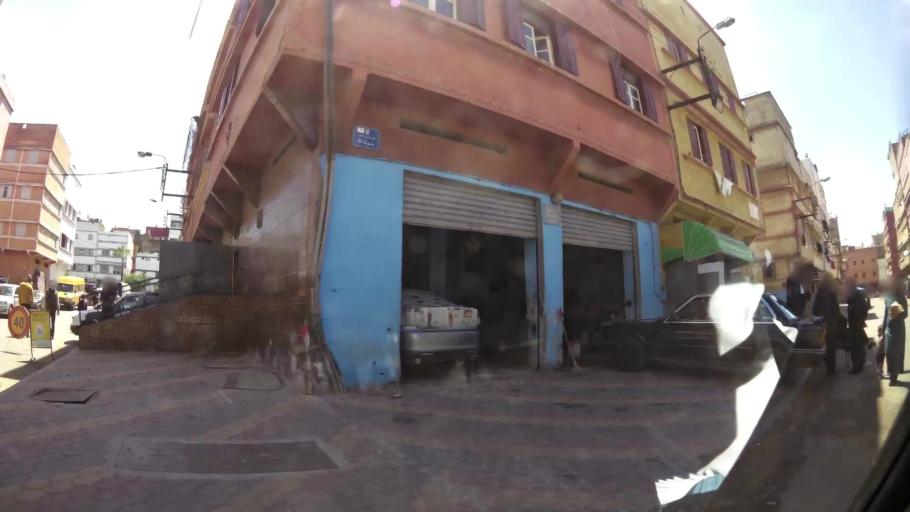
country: MA
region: Grand Casablanca
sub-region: Casablanca
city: Casablanca
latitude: 33.5631
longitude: -7.5717
